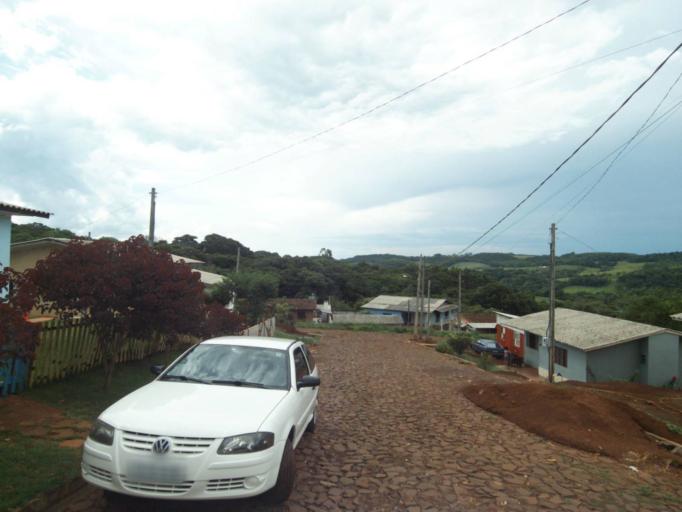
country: BR
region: Parana
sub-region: Guaraniacu
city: Guaraniacu
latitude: -25.0940
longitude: -52.8712
